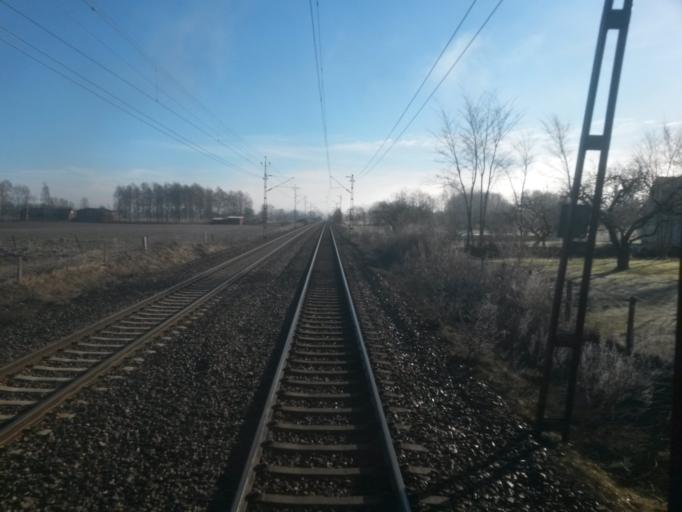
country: SE
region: Vaestra Goetaland
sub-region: Herrljunga Kommun
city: Herrljunga
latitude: 58.0681
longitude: 12.9717
